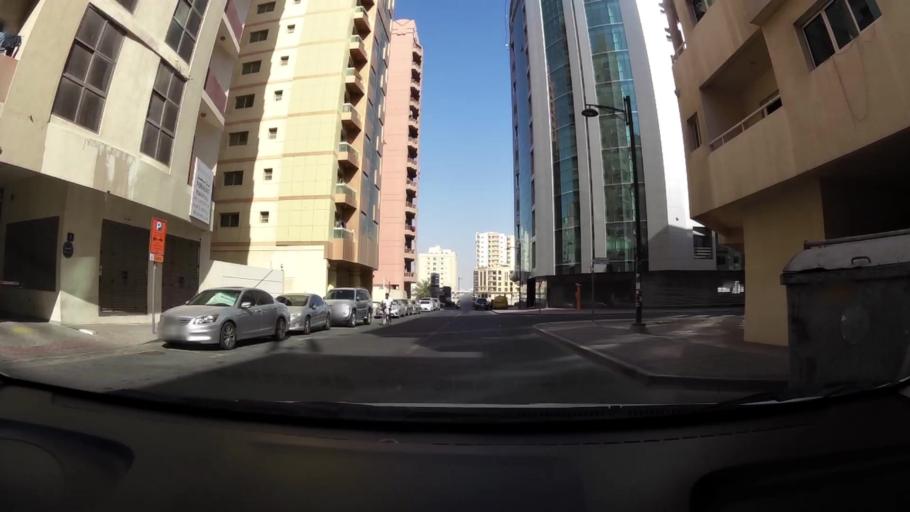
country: AE
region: Ash Shariqah
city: Sharjah
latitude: 25.2949
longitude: 55.3813
